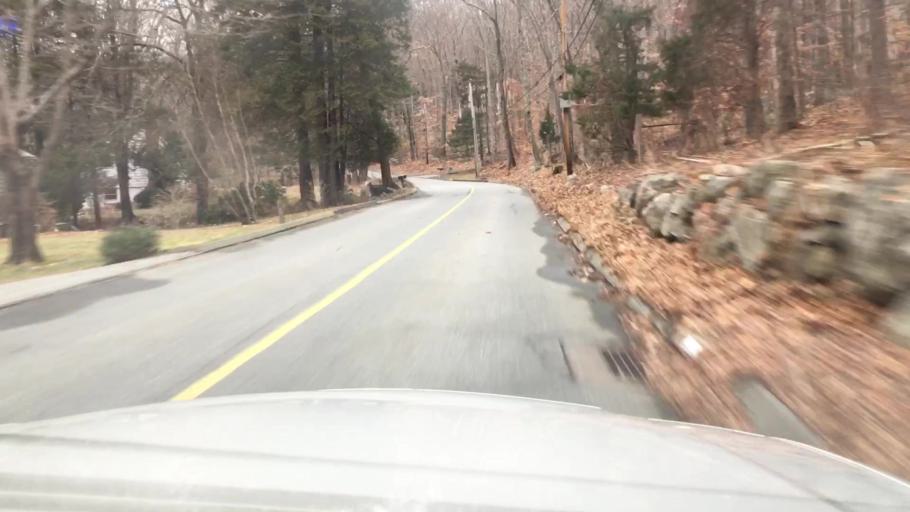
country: US
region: Connecticut
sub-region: Middlesex County
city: Essex Village
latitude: 41.3672
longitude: -72.4013
